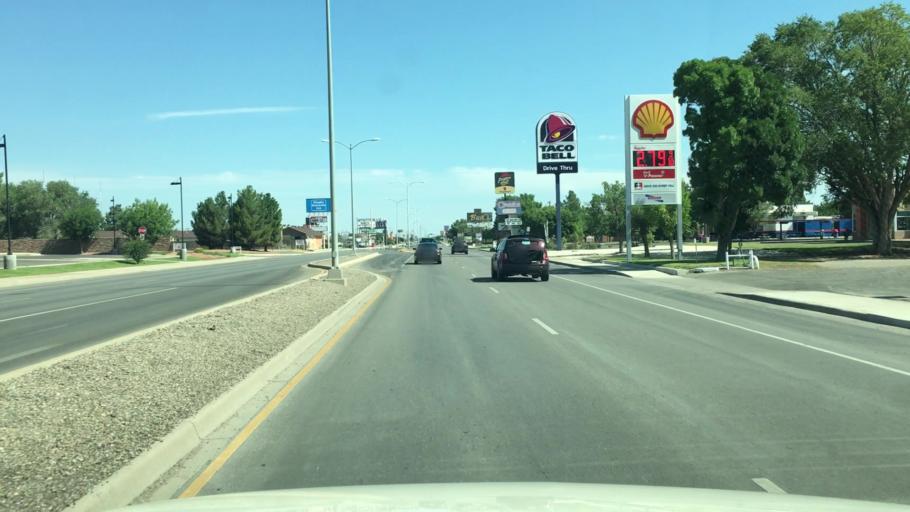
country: US
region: New Mexico
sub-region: Chaves County
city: Roswell
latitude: 33.4324
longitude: -104.5231
